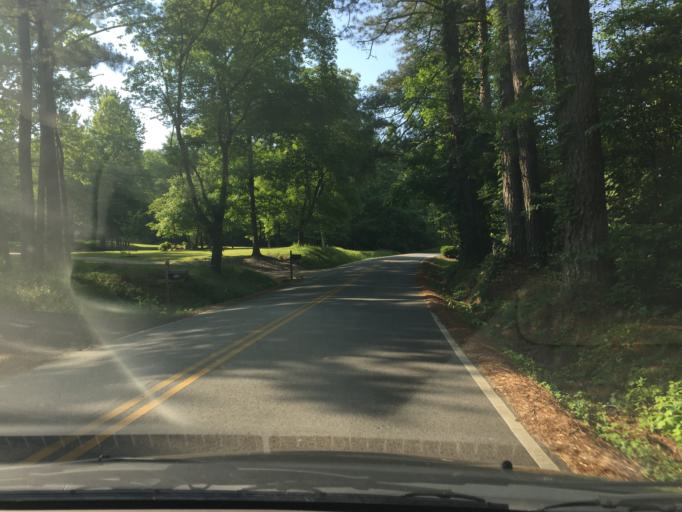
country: US
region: Tennessee
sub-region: Hamilton County
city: Apison
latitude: 35.0441
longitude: -85.0162
